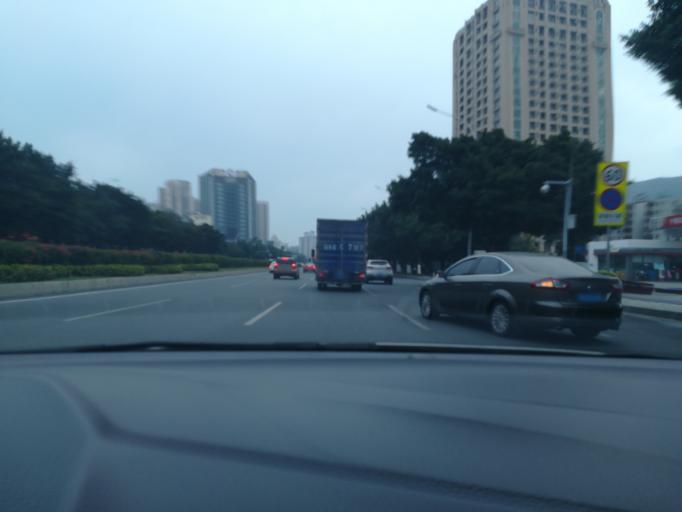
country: CN
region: Guangdong
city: Nansha
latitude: 22.8030
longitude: 113.5460
